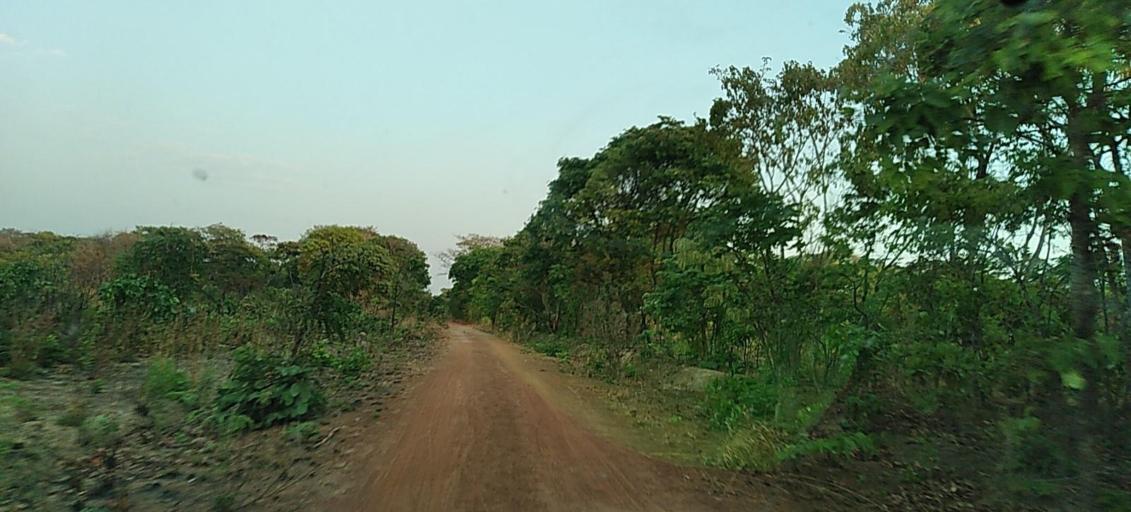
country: ZM
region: North-Western
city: Kalengwa
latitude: -13.1173
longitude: 25.1723
